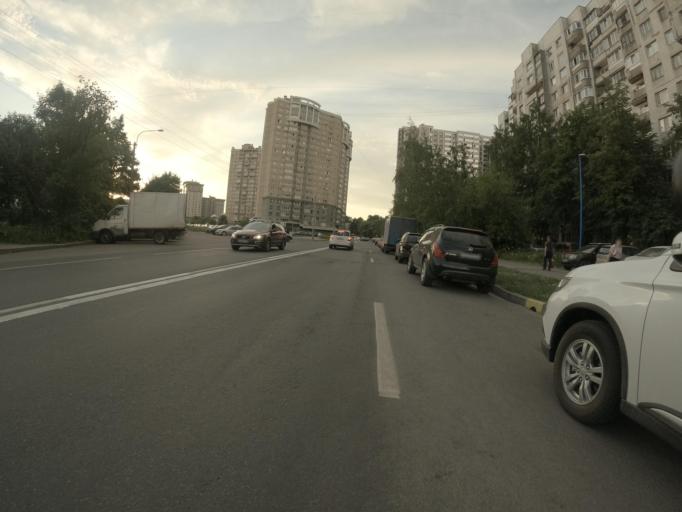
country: RU
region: St.-Petersburg
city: Kupchino
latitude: 59.8391
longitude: 30.3109
